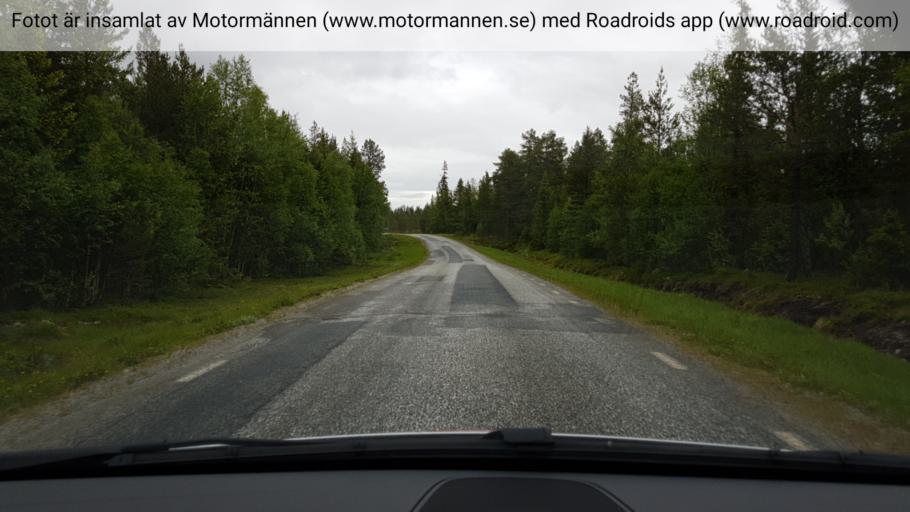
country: SE
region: Jaemtland
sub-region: Harjedalens Kommun
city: Sveg
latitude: 62.3469
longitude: 13.4438
